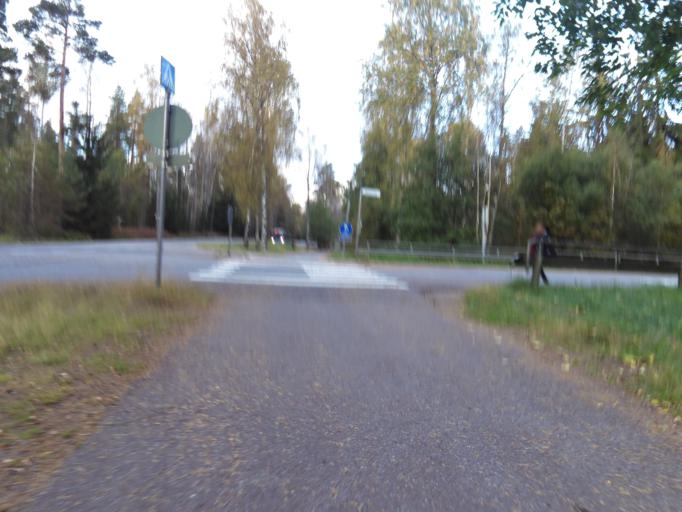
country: FI
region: Uusimaa
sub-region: Helsinki
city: Kauniainen
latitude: 60.2857
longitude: 24.7464
